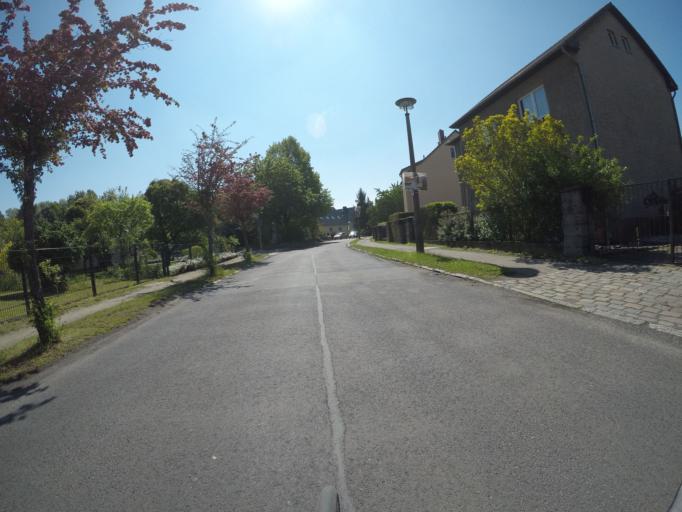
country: DE
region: Berlin
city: Fennpfuhl
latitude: 52.5371
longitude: 13.4562
